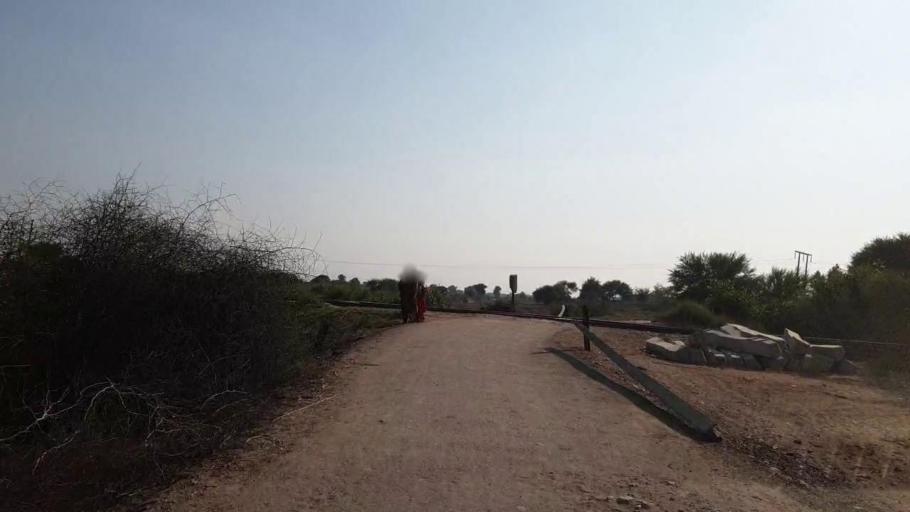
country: PK
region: Sindh
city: Sehwan
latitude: 26.4465
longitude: 67.8145
